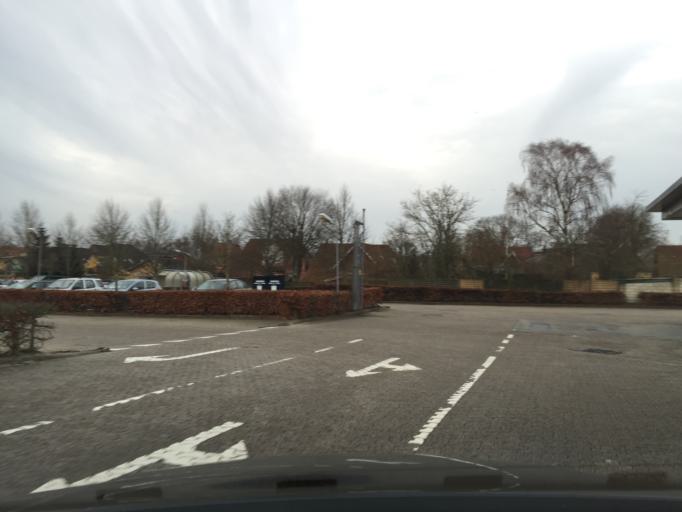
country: DK
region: Central Jutland
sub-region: Viborg Kommune
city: Bjerringbro
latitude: 56.3759
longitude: 9.6545
